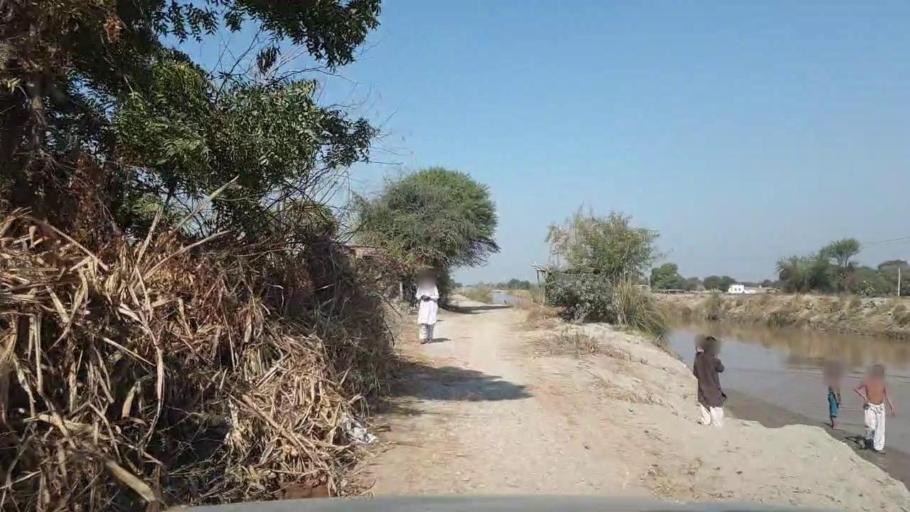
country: PK
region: Sindh
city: Tando Allahyar
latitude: 25.4253
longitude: 68.6472
